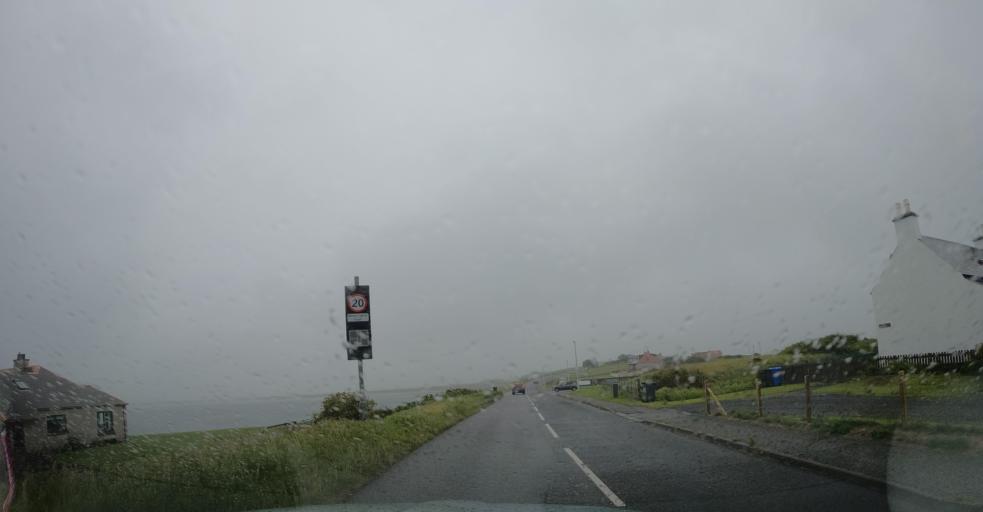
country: GB
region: Scotland
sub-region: Eilean Siar
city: Benbecula
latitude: 57.4744
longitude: -7.3865
